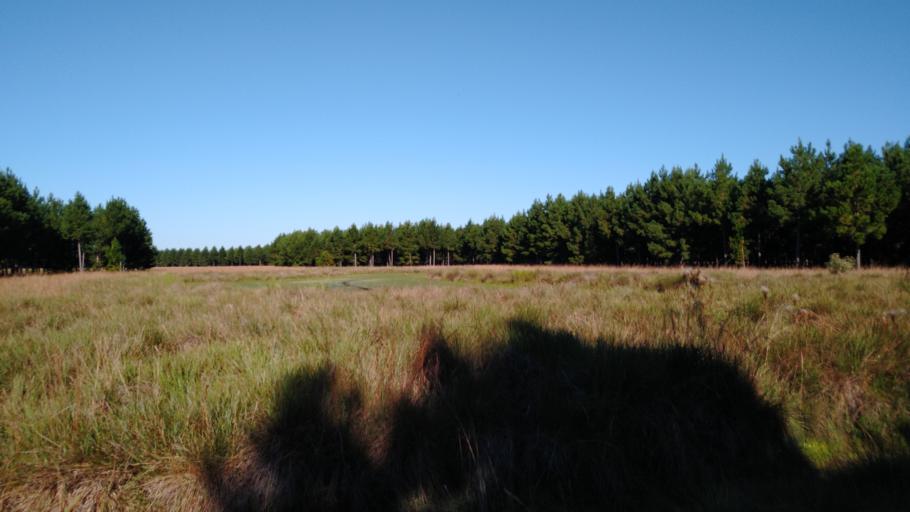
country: AR
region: Corrientes
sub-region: Departamento de San Miguel
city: San Miguel
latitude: -28.1968
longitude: -57.5596
